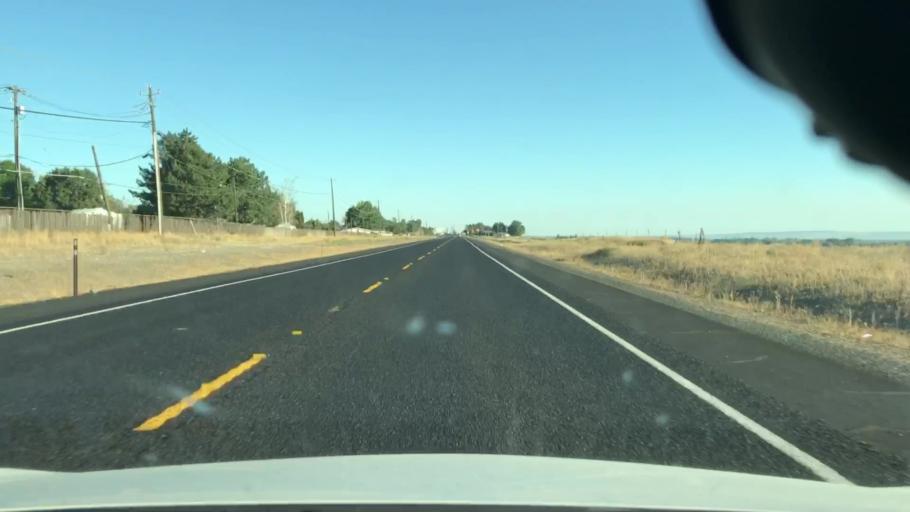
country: US
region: Washington
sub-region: Grant County
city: Moses Lake North
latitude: 47.1699
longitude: -119.3283
